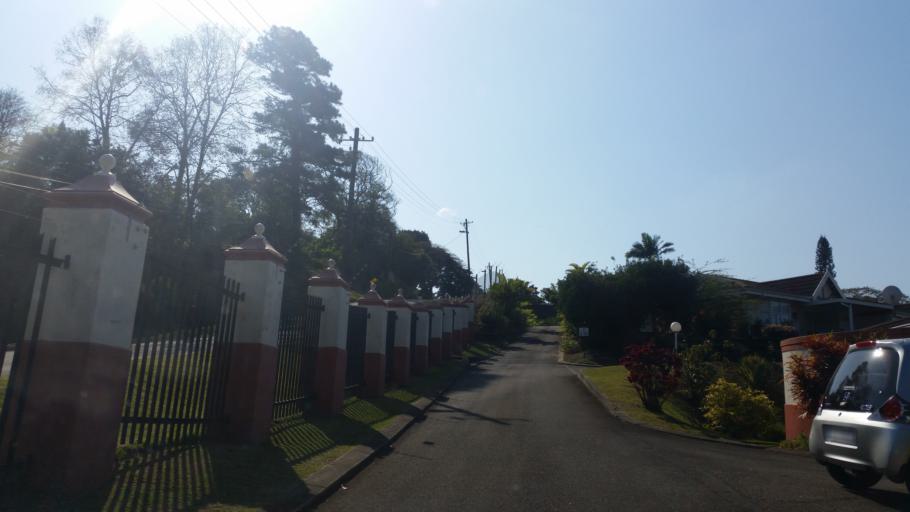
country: ZA
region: KwaZulu-Natal
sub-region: eThekwini Metropolitan Municipality
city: Berea
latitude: -29.8488
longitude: 30.8998
